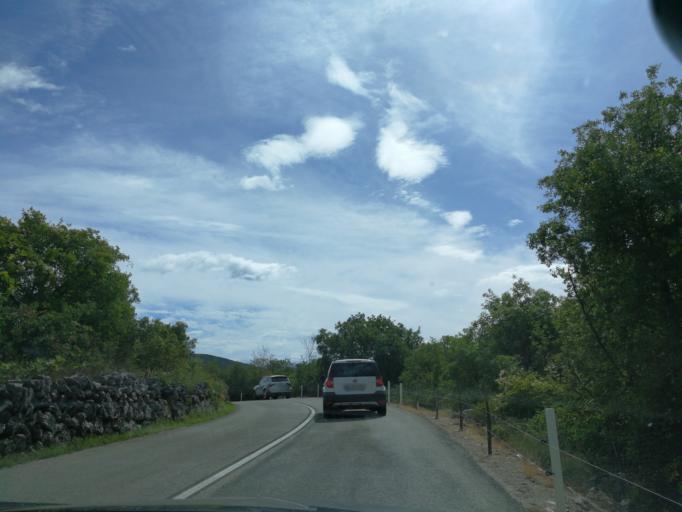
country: HR
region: Primorsko-Goranska
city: Punat
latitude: 45.0798
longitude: 14.6538
